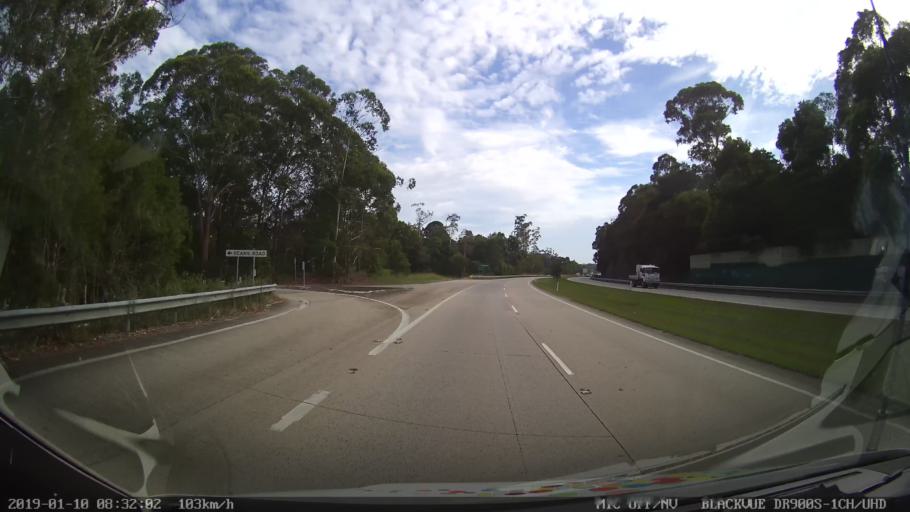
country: AU
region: New South Wales
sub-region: Coffs Harbour
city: Boambee
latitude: -30.3480
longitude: 153.0656
